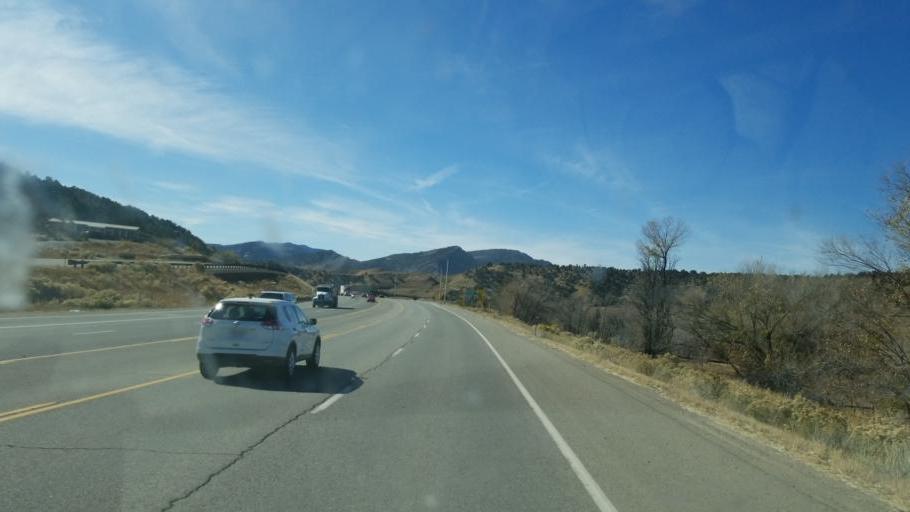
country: US
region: Colorado
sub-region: La Plata County
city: Durango
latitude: 37.2292
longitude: -107.8301
